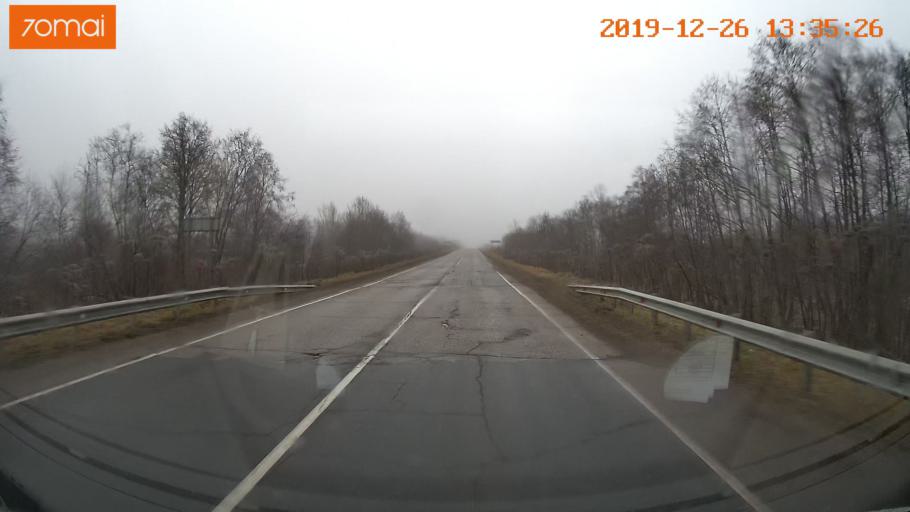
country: RU
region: Vologda
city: Sheksna
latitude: 58.7928
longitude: 38.3410
